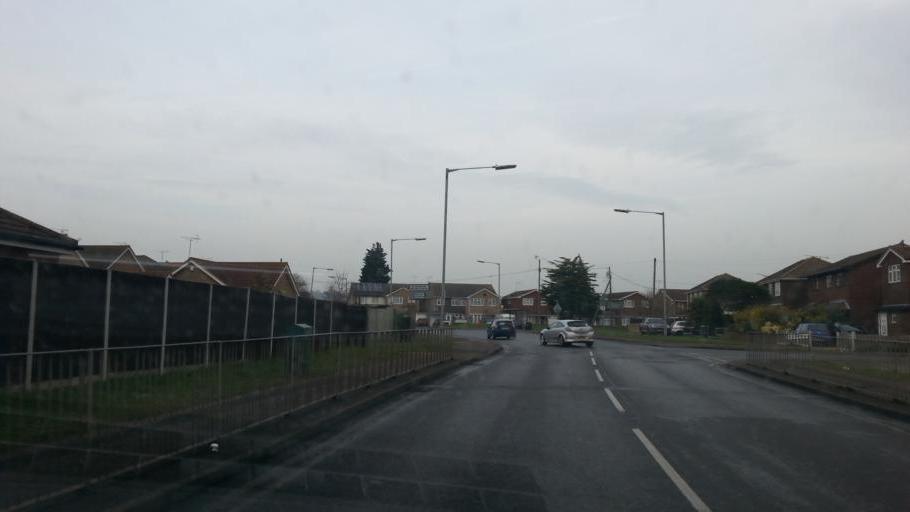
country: GB
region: England
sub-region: Essex
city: Canvey Island
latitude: 51.5302
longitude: 0.5794
